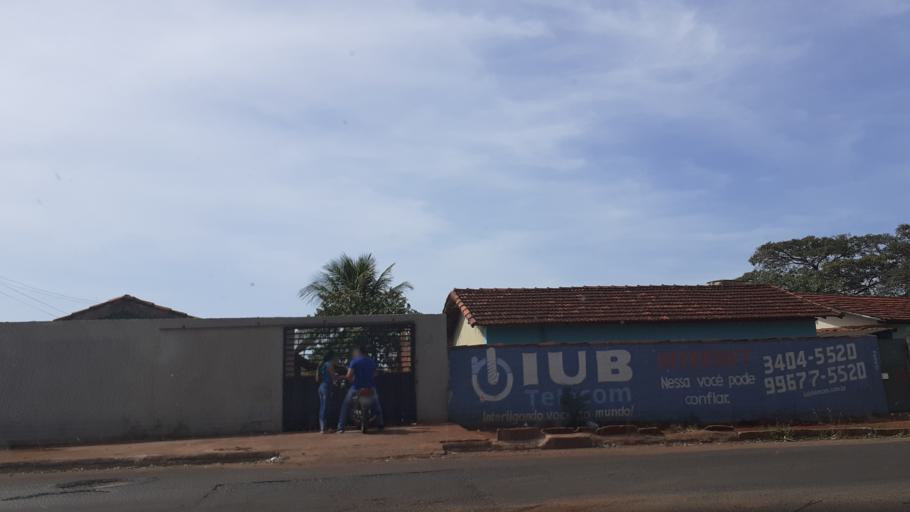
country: BR
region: Goias
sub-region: Itumbiara
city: Itumbiara
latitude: -18.4131
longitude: -49.2301
